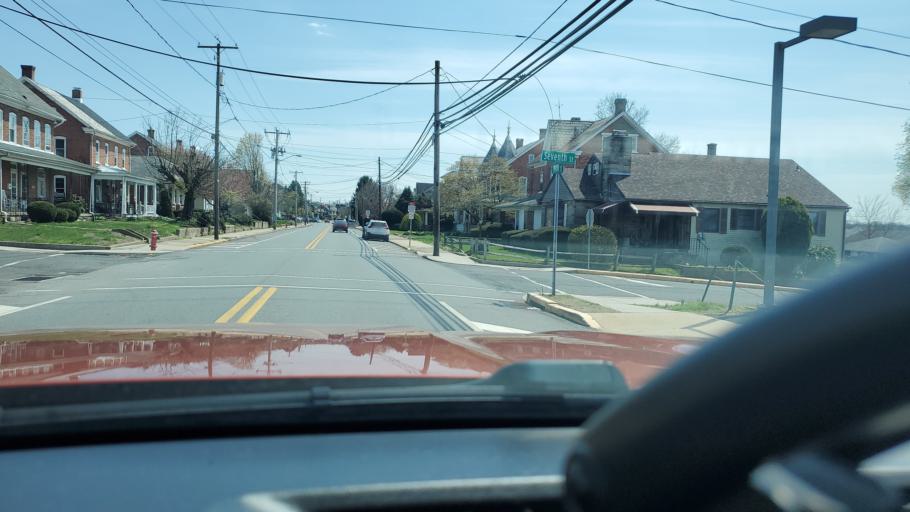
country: US
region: Pennsylvania
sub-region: Montgomery County
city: Red Hill
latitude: 40.3795
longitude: -75.4846
